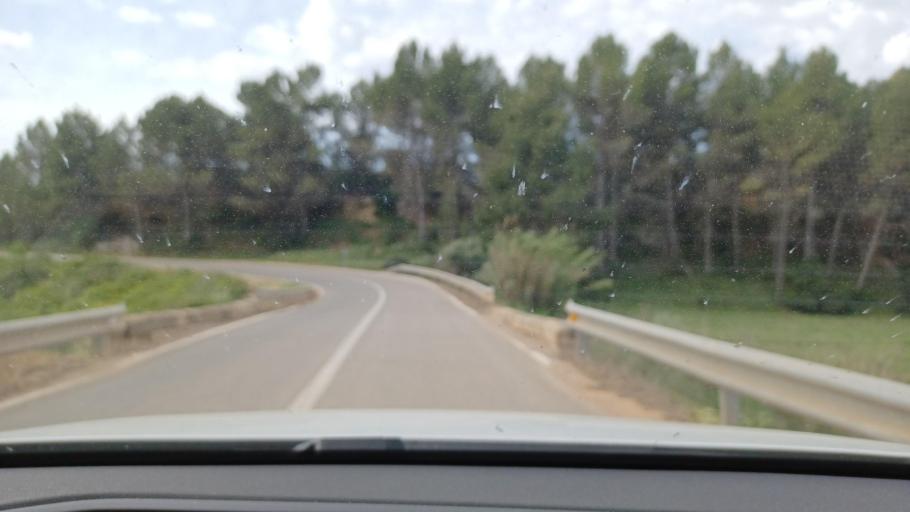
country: ES
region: Catalonia
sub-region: Provincia de Tarragona
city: Bot
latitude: 41.0177
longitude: 0.3847
